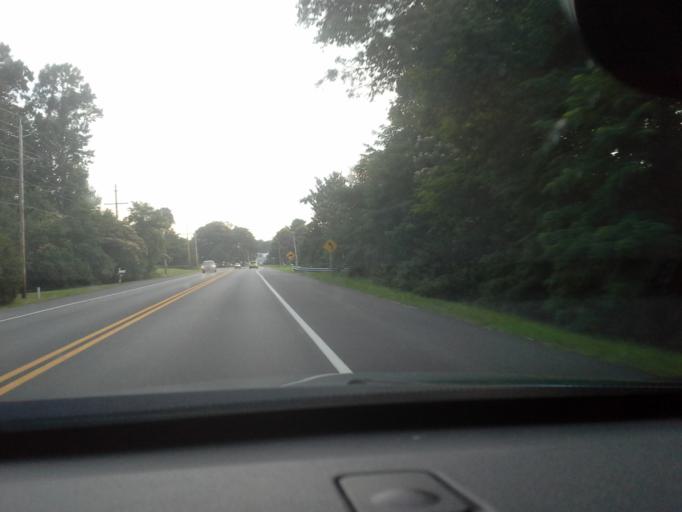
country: US
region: Maryland
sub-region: Calvert County
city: Prince Frederick
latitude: 38.5529
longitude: -76.5747
